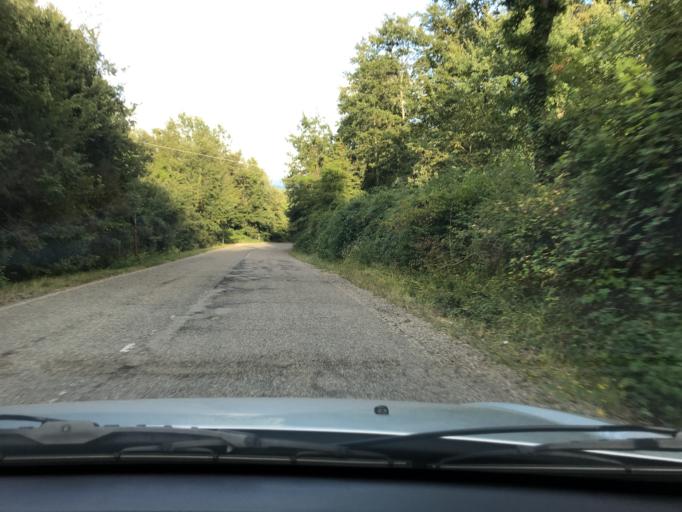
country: IT
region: Umbria
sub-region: Provincia di Terni
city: Guardea
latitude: 42.6474
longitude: 12.3521
